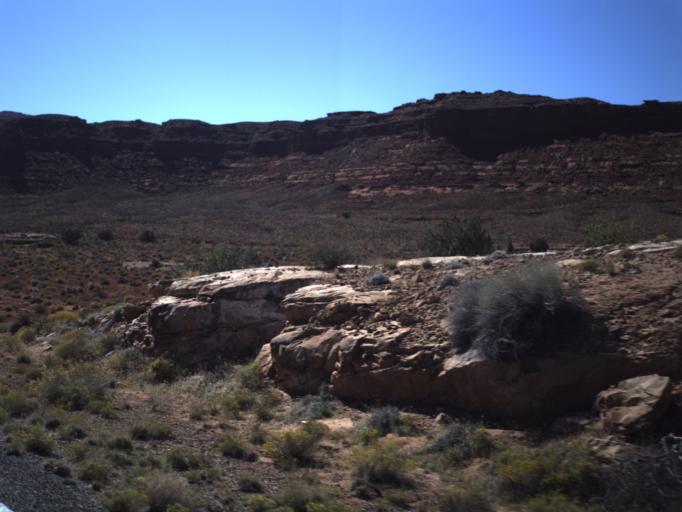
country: US
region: Utah
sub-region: San Juan County
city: Blanding
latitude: 37.8140
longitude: -110.3433
